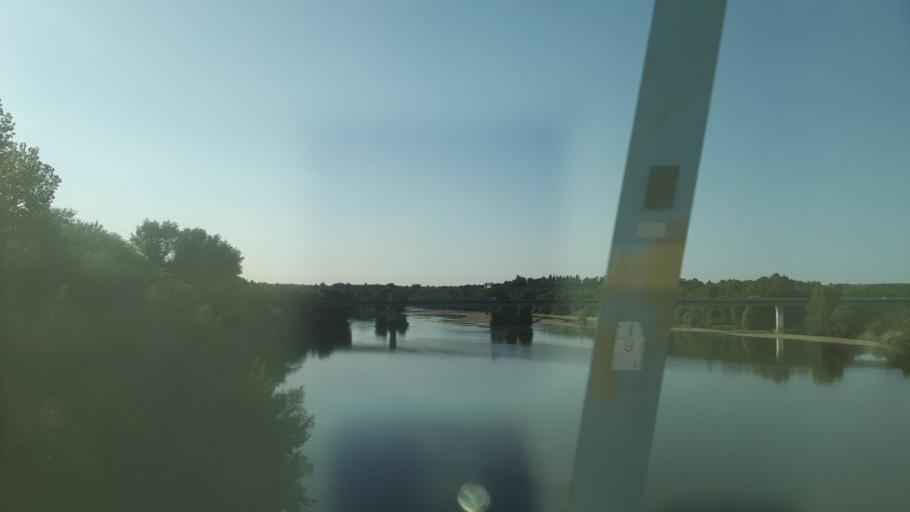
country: FR
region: Centre
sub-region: Departement d'Indre-et-Loire
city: Vouvray
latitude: 47.3996
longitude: 0.8038
